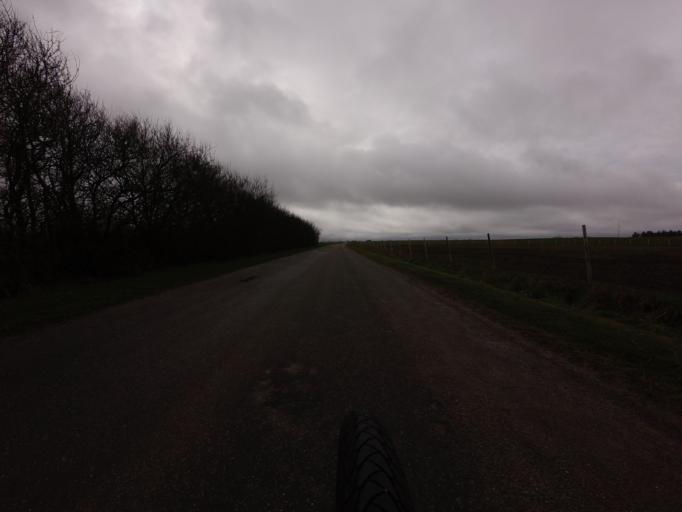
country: DK
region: North Denmark
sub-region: Hjorring Kommune
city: Vra
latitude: 57.3792
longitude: 9.8387
